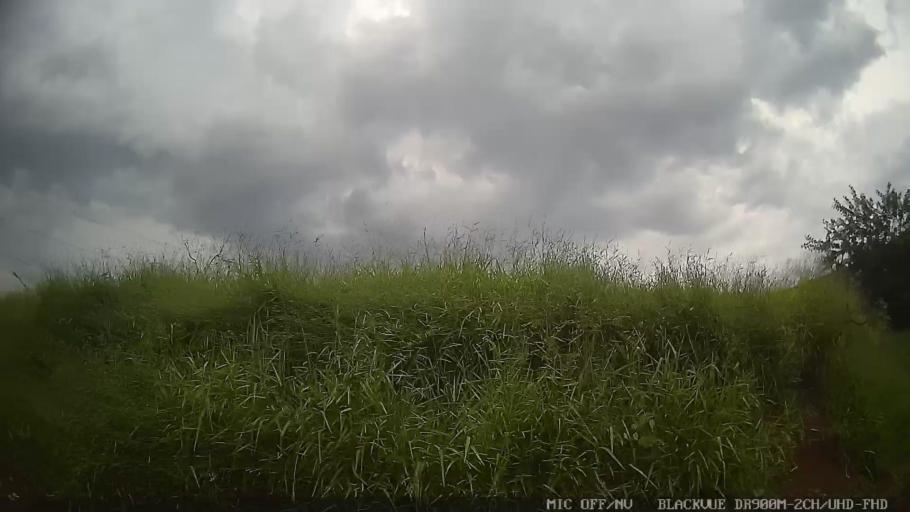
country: BR
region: Sao Paulo
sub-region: Itaquaquecetuba
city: Itaquaquecetuba
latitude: -23.4528
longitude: -46.3192
